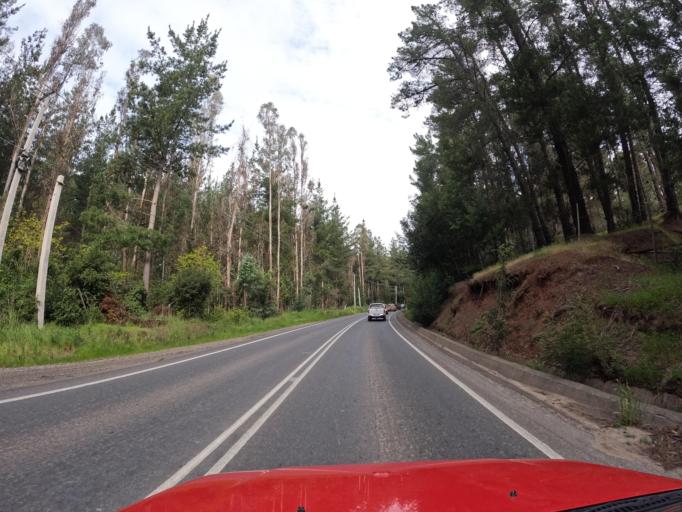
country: CL
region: O'Higgins
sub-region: Provincia de Colchagua
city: Santa Cruz
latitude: -34.3552
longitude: -71.9036
